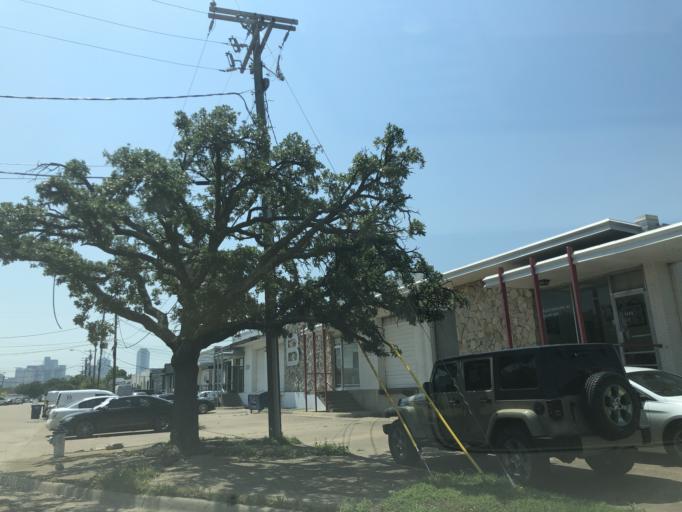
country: US
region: Texas
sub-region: Dallas County
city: Dallas
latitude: 32.8000
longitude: -96.8361
